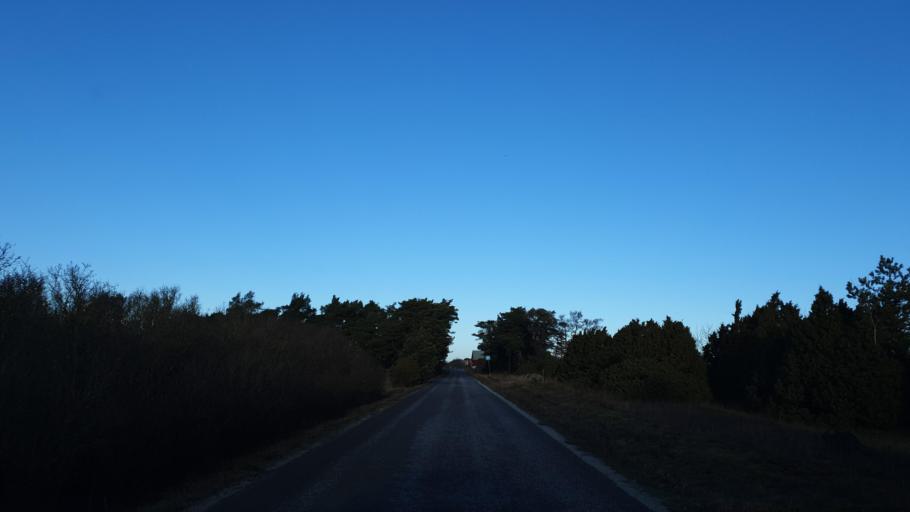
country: SE
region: Gotland
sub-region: Gotland
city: Slite
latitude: 57.3917
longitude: 18.8087
